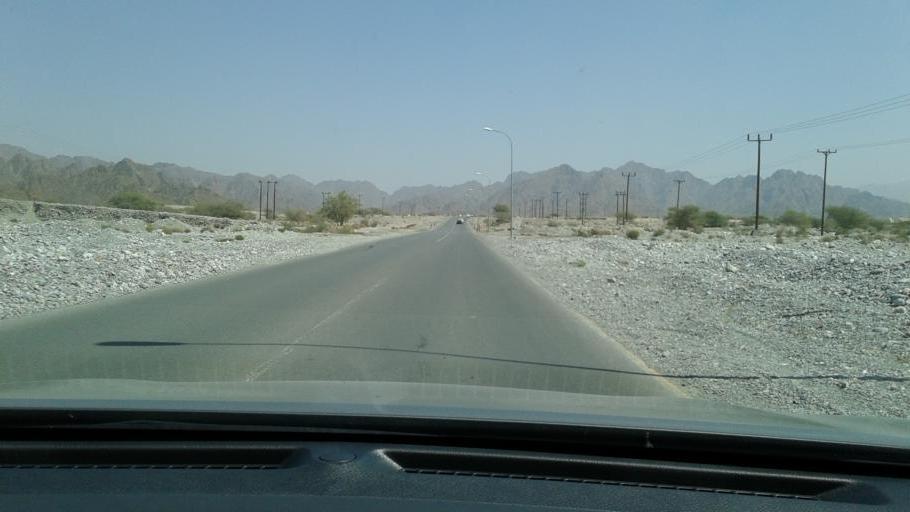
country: OM
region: Al Batinah
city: Rustaq
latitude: 23.3679
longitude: 57.4620
